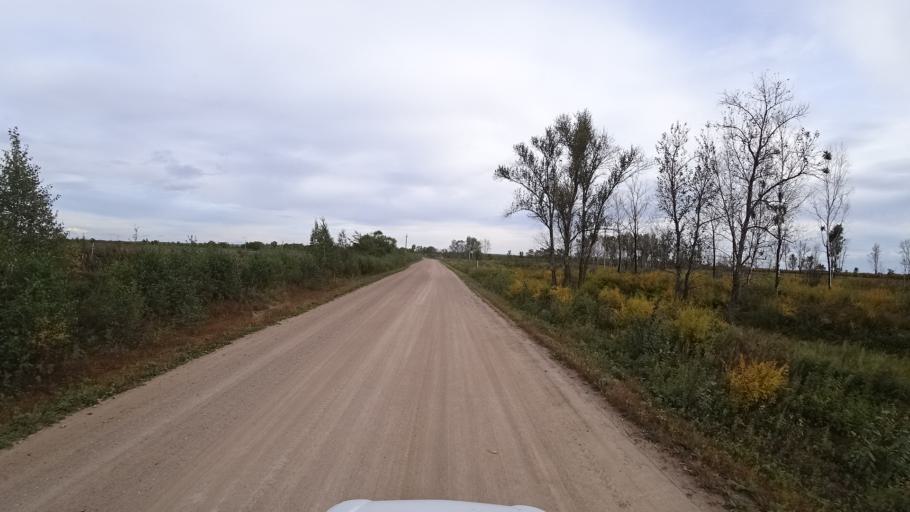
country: RU
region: Amur
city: Arkhara
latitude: 49.3784
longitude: 130.1778
